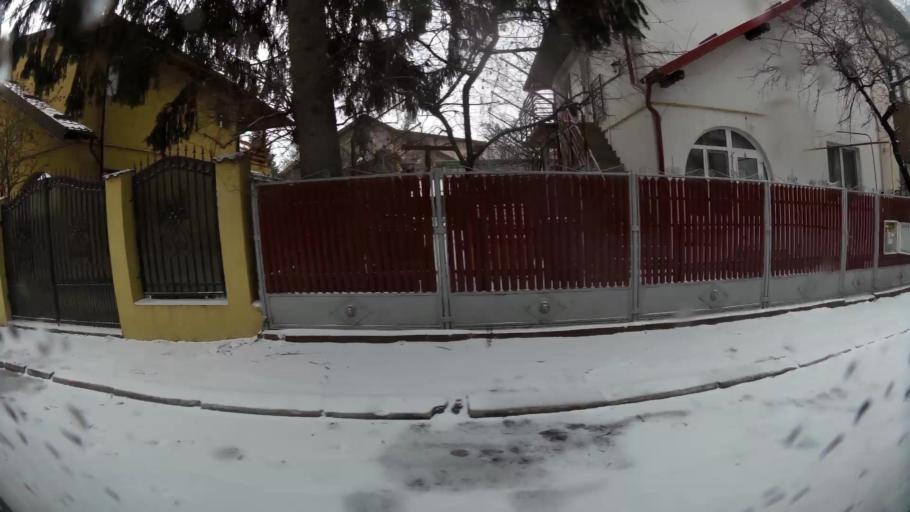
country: RO
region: Prahova
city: Ploiesti
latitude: 44.9294
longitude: 26.0074
